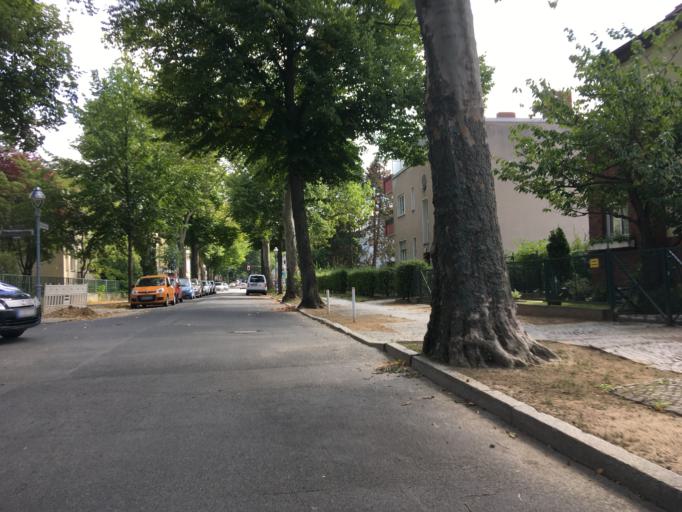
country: DE
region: Berlin
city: Marienfelde
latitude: 52.4231
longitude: 13.3686
